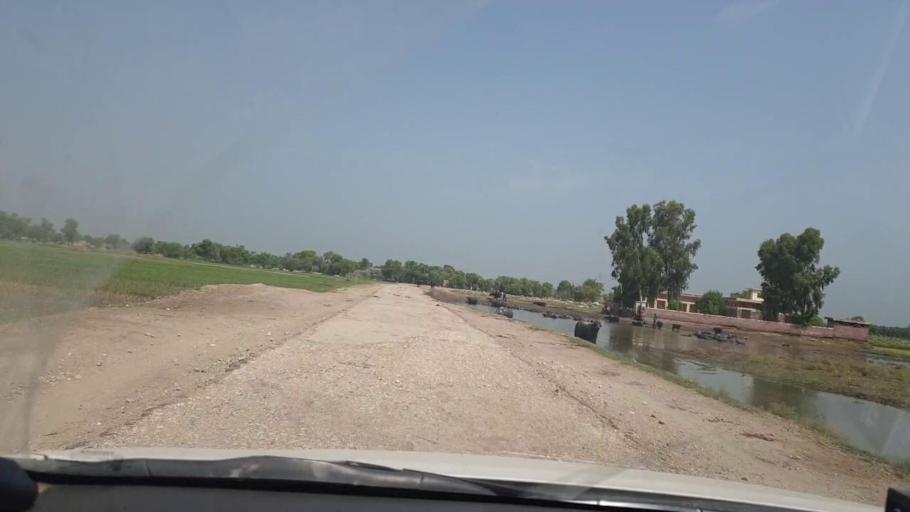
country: PK
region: Sindh
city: Chak
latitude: 27.8776
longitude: 68.7831
